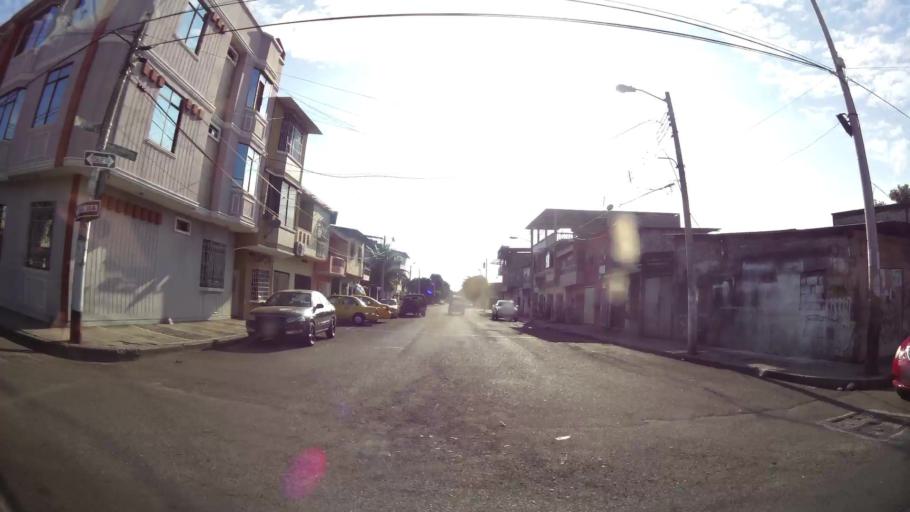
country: EC
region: Guayas
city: Guayaquil
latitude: -2.2175
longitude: -79.9032
